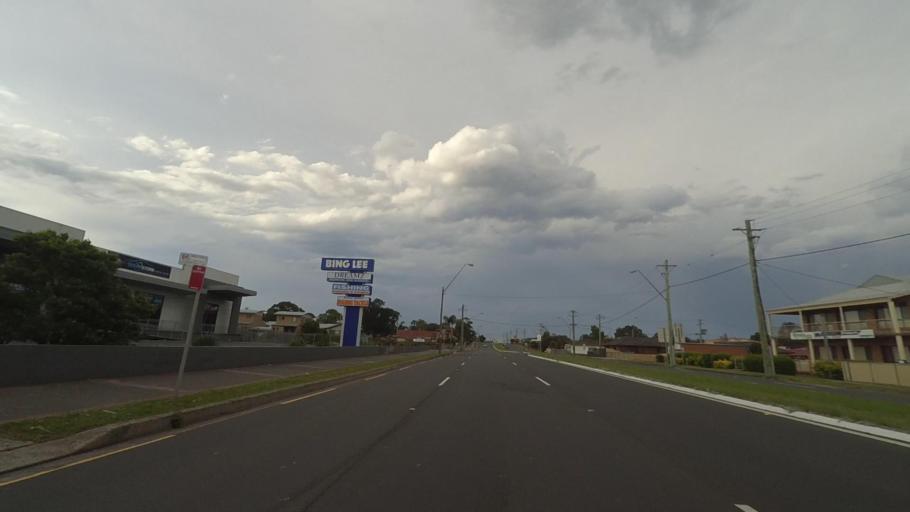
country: AU
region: New South Wales
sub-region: Shellharbour
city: Lake Illawarra
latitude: -34.5518
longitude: 150.8601
